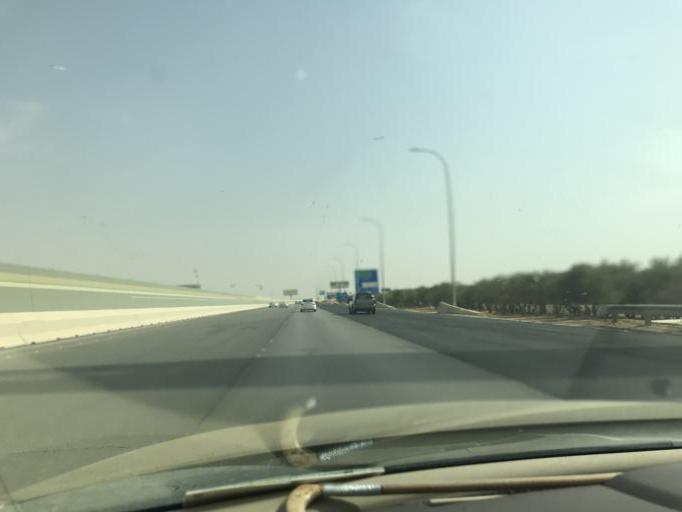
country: SA
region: Ar Riyad
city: Riyadh
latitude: 24.9236
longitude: 46.7201
